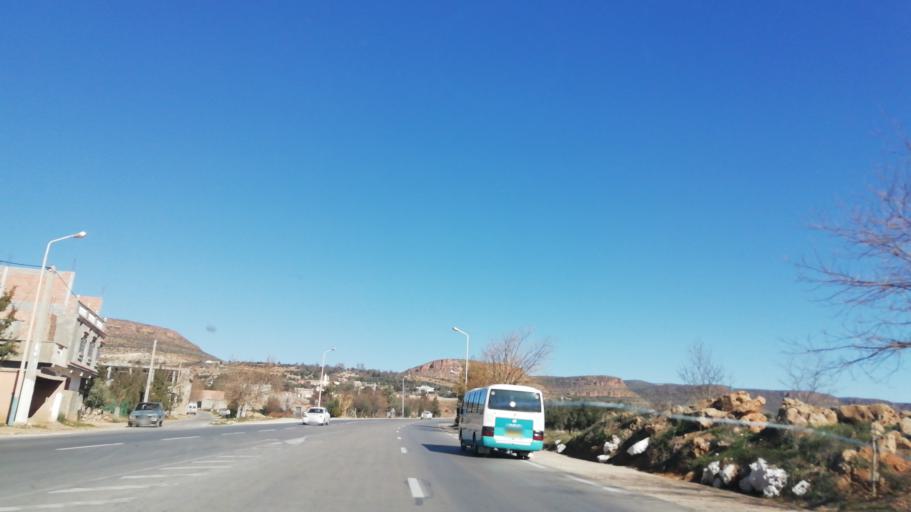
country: DZ
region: Tlemcen
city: Sebdou
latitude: 34.6721
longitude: -1.3181
